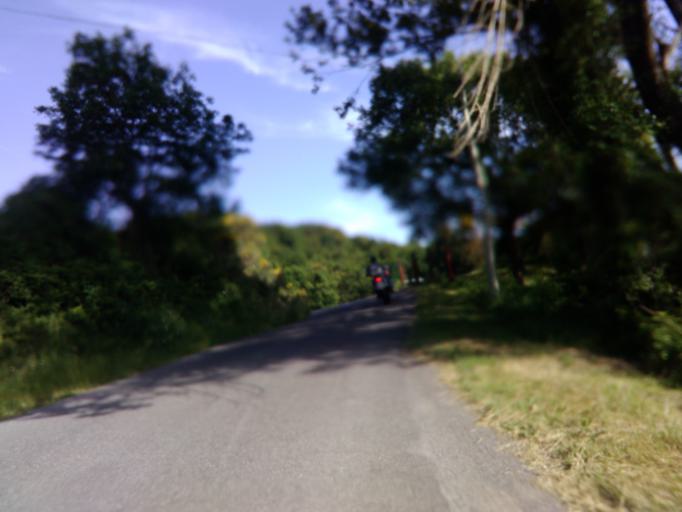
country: IT
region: Tuscany
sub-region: Provincia di Massa-Carrara
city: Fosdinovo
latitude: 44.1509
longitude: 10.0203
